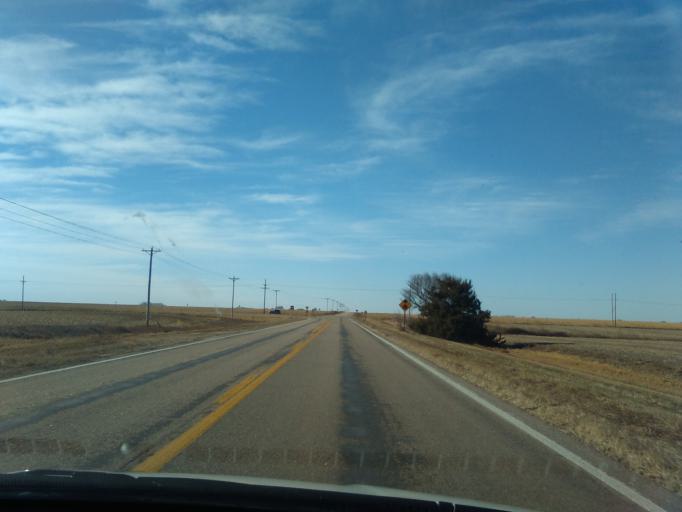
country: US
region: Nebraska
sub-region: Clay County
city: Harvard
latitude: 40.6115
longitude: -98.1059
